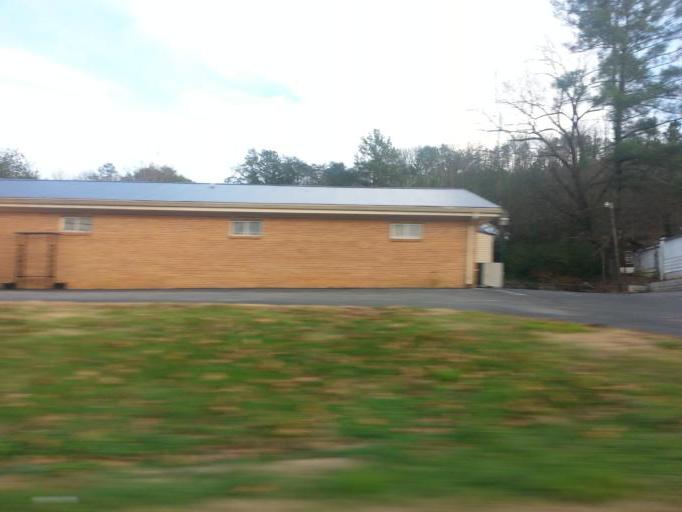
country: US
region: Tennessee
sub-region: Rhea County
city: Dayton
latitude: 35.5058
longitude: -85.0014
